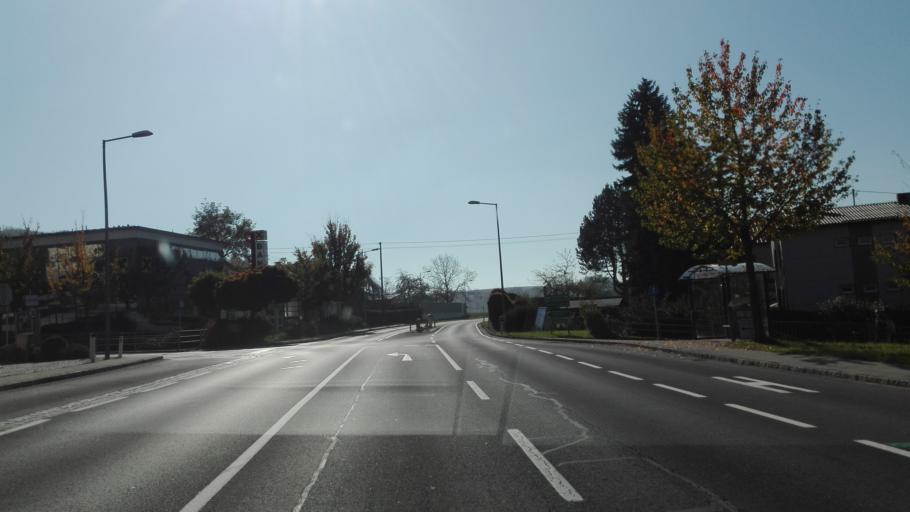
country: AT
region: Upper Austria
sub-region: Politischer Bezirk Urfahr-Umgebung
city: Ottensheim
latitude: 48.2994
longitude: 14.1664
